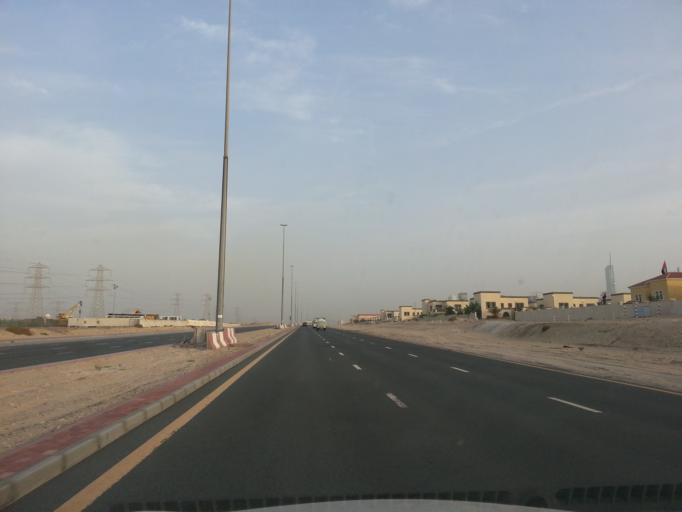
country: AE
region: Dubai
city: Dubai
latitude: 25.0454
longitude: 55.1503
